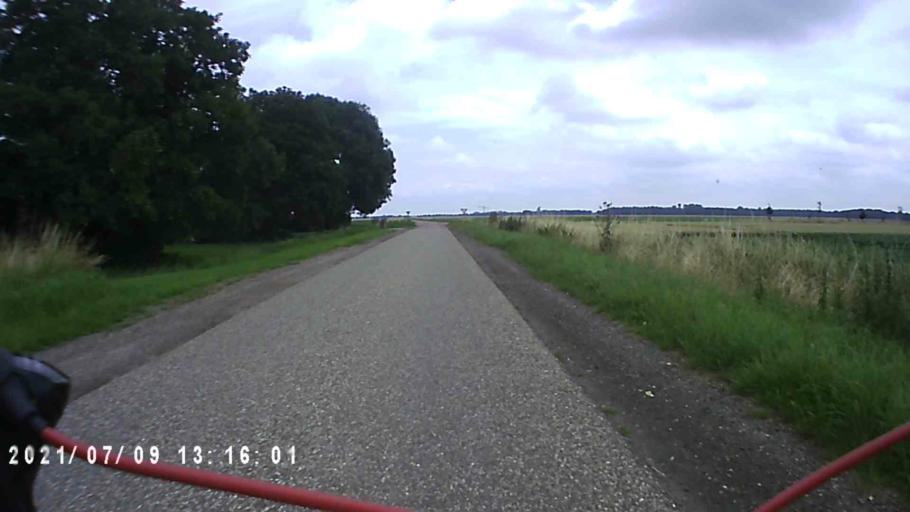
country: NL
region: Groningen
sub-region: Gemeente Vlagtwedde
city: Vlagtwedde
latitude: 53.1208
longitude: 7.1436
